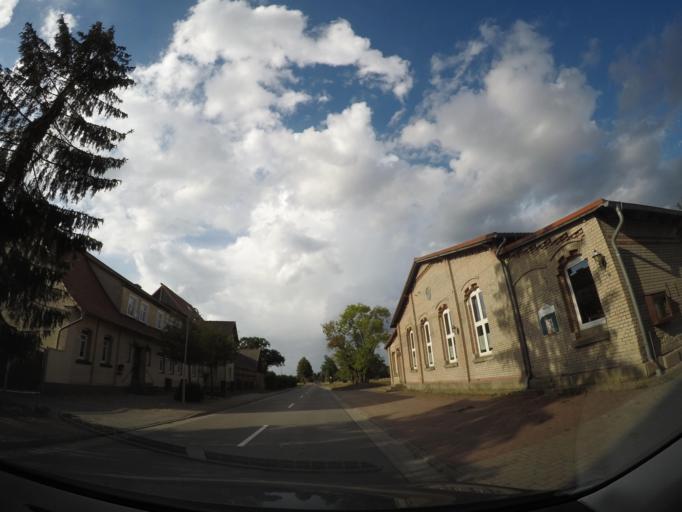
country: DE
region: Saxony-Anhalt
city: Mieste
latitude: 52.4759
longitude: 11.2618
